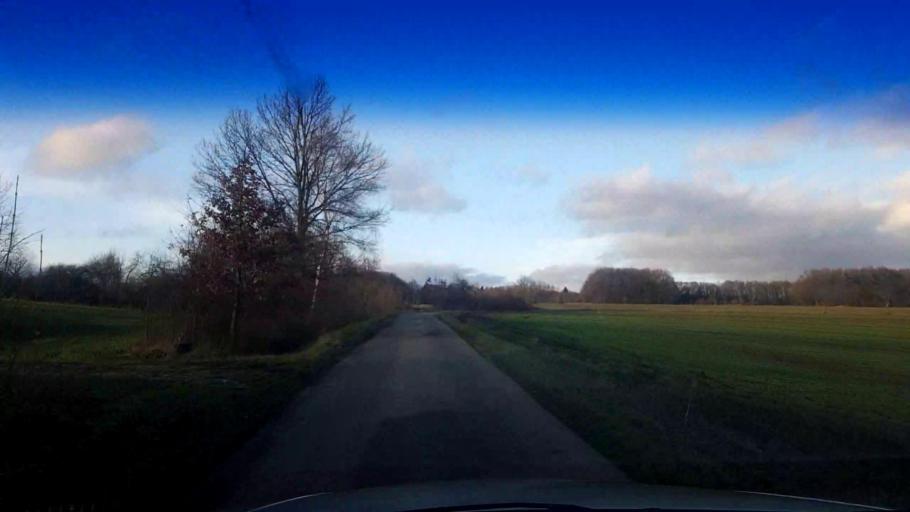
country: DE
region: Bavaria
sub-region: Upper Franconia
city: Buttenheim
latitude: 49.8140
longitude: 11.0373
